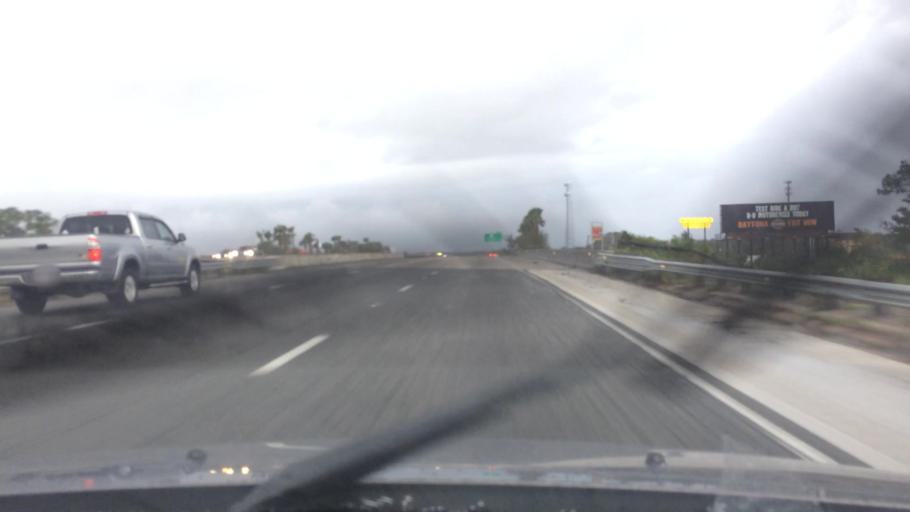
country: US
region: Florida
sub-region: Volusia County
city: Ormond-by-the-Sea
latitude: 29.3322
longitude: -81.1310
